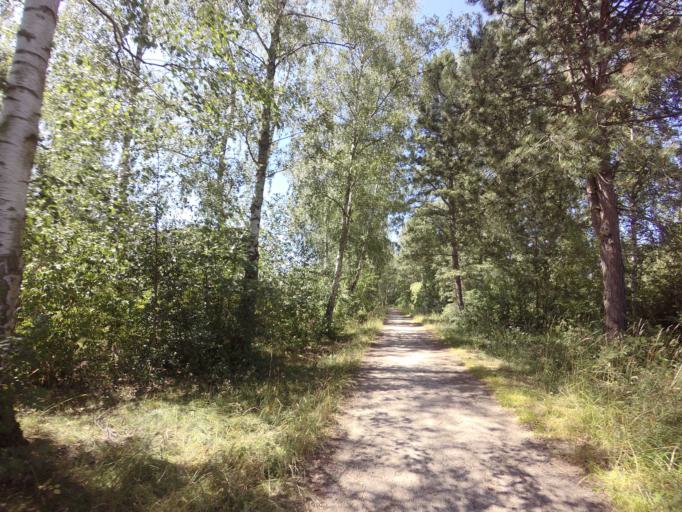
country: SE
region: Skane
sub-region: Vellinge Kommun
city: Skanor med Falsterbo
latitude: 55.4051
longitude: 12.8575
